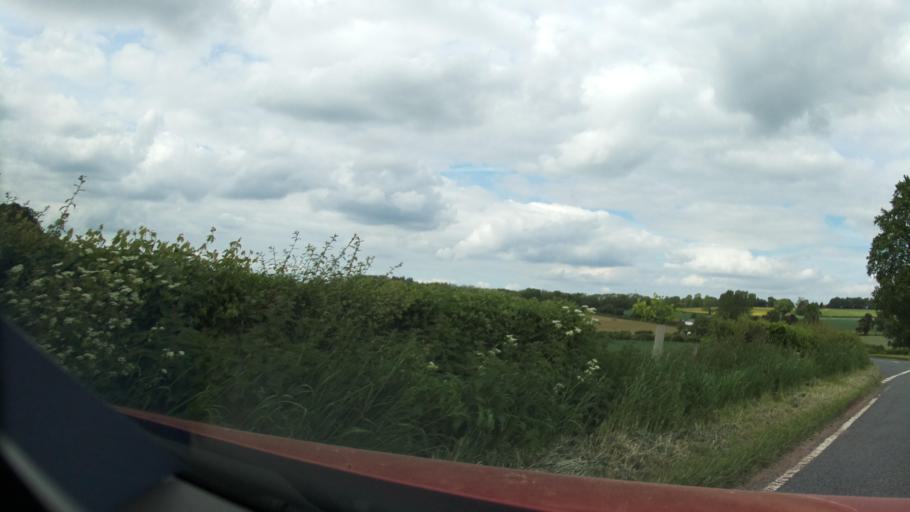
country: GB
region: England
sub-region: Herefordshire
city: Yatton
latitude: 51.9510
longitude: -2.5420
